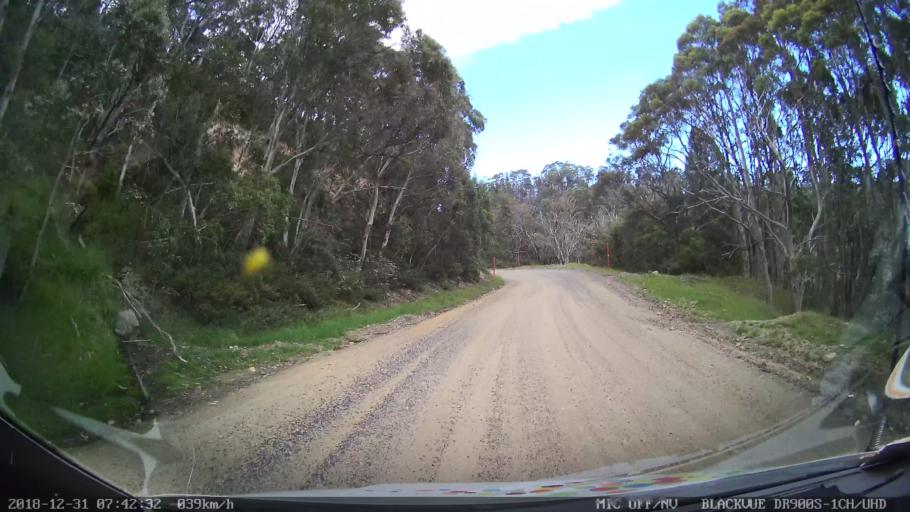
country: AU
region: New South Wales
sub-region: Snowy River
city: Jindabyne
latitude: -36.3572
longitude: 148.4090
